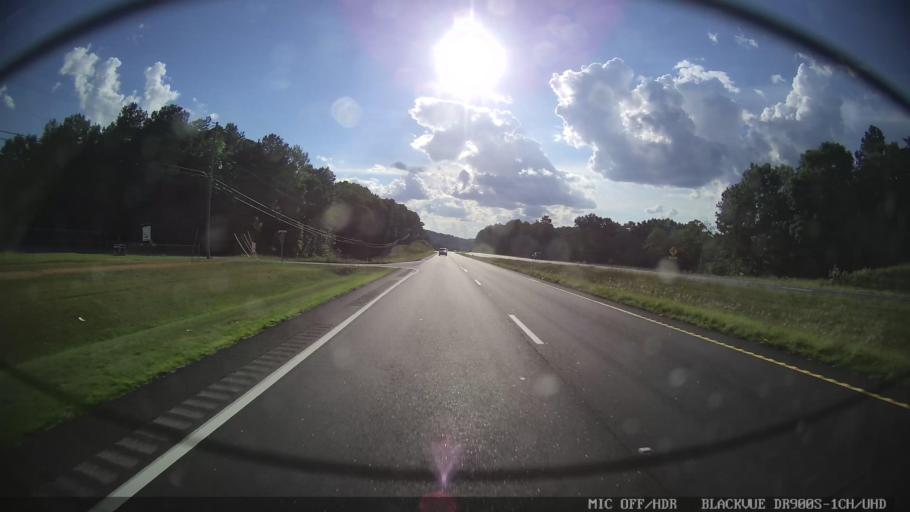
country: US
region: Georgia
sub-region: Floyd County
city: Rome
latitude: 34.2145
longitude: -85.1097
